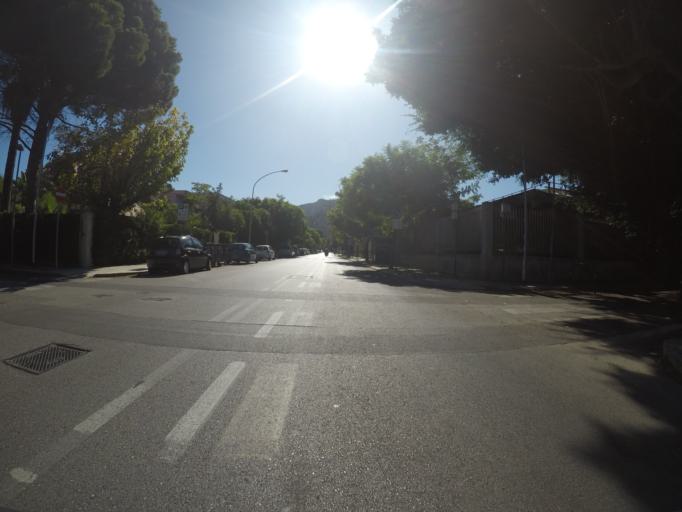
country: IT
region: Sicily
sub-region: Palermo
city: Palermo
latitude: 38.1990
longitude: 13.3278
